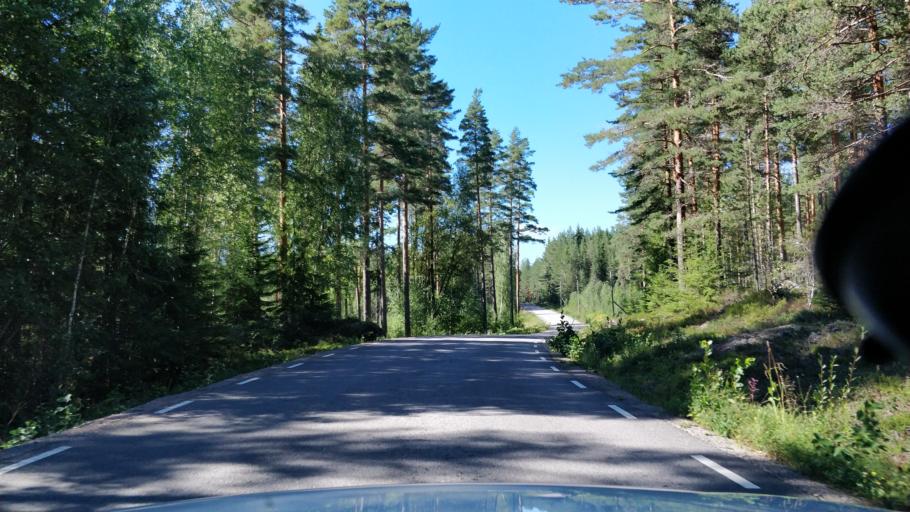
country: SE
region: Dalarna
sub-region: Faluns Kommun
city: Bjursas
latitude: 60.7423
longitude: 15.5367
